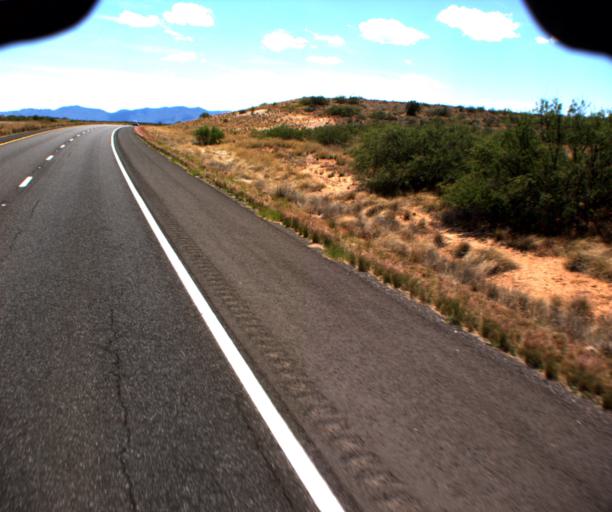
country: US
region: Arizona
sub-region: Yavapai County
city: Cornville
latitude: 34.7777
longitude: -111.9288
